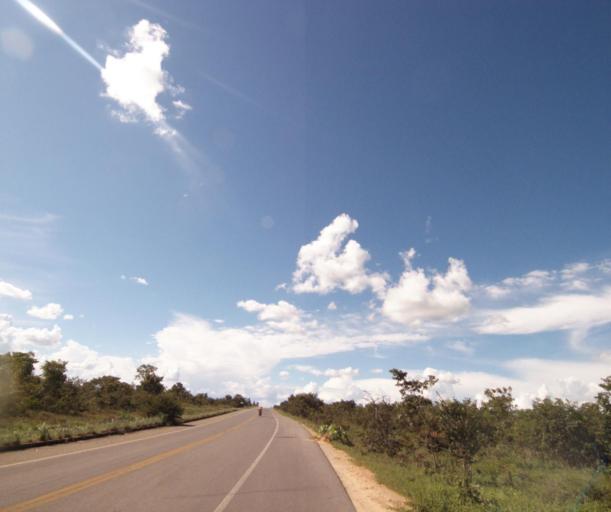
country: BR
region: Bahia
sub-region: Correntina
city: Correntina
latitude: -13.3095
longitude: -44.6419
